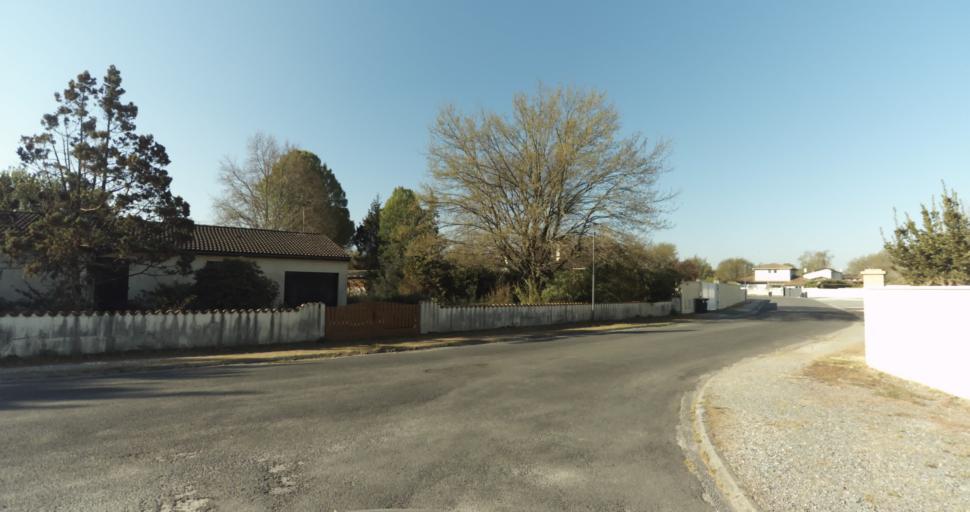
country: FR
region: Aquitaine
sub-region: Departement de la Gironde
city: Martignas-sur-Jalle
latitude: 44.8108
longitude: -0.7869
